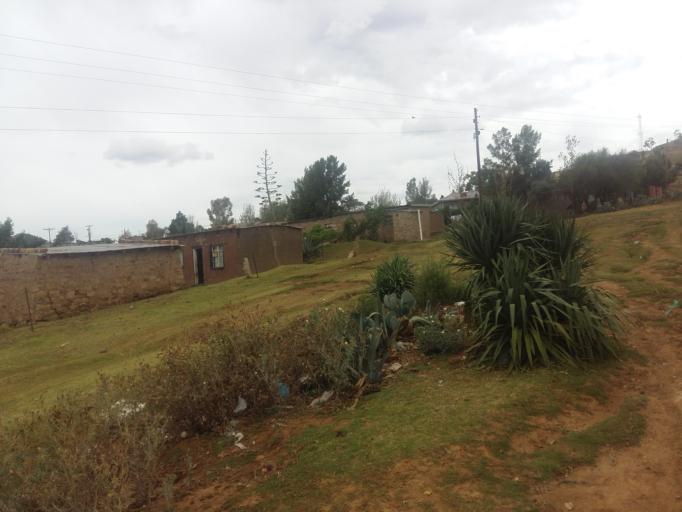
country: LS
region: Mafeteng
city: Mafeteng
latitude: -29.7004
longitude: 27.4338
